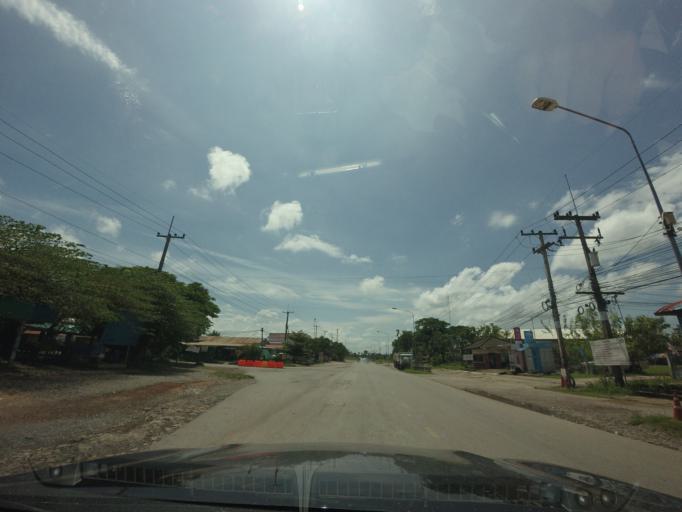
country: TH
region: Nong Khai
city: Pho Tak
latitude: 17.7766
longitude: 102.3952
